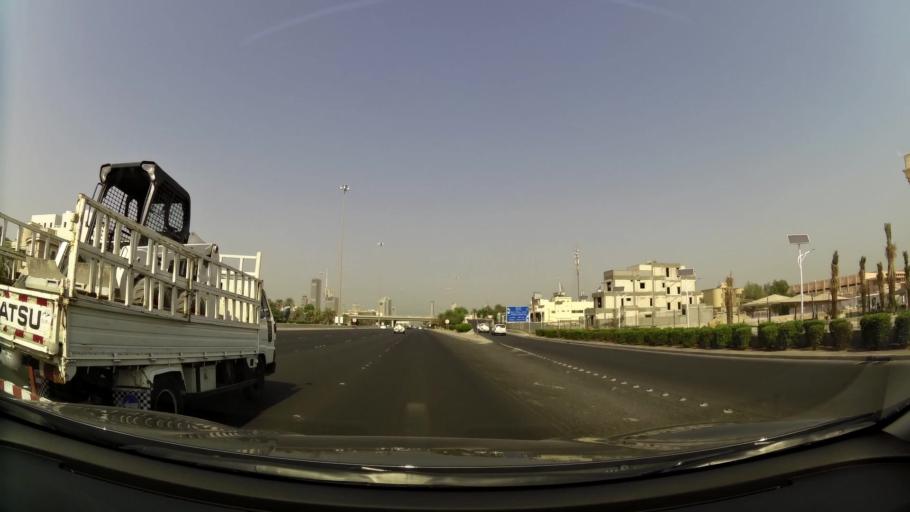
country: KW
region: Al Asimah
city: Ad Dasmah
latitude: 29.3480
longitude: 47.9958
